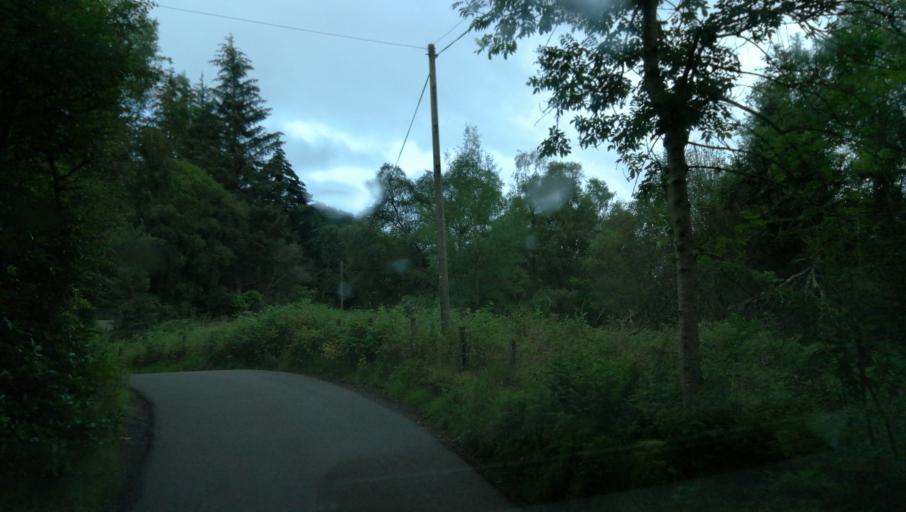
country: GB
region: Scotland
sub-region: Perth and Kinross
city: Blairgowrie
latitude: 56.6923
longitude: -3.4029
